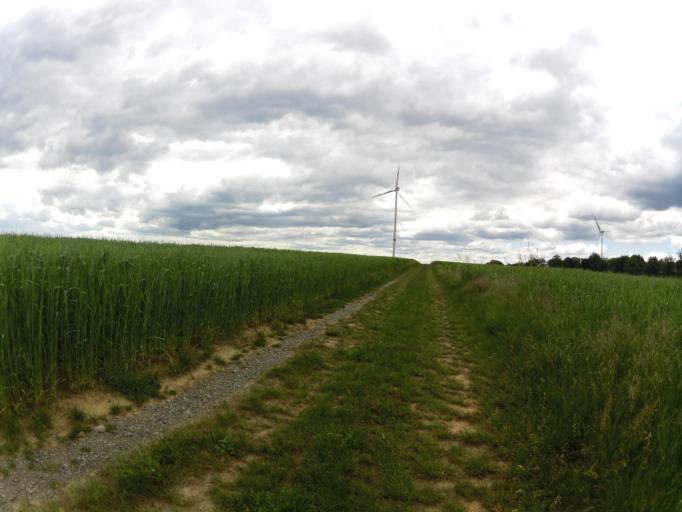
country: DE
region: Bavaria
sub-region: Regierungsbezirk Unterfranken
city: Guntersleben
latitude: 49.8789
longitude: 9.8861
